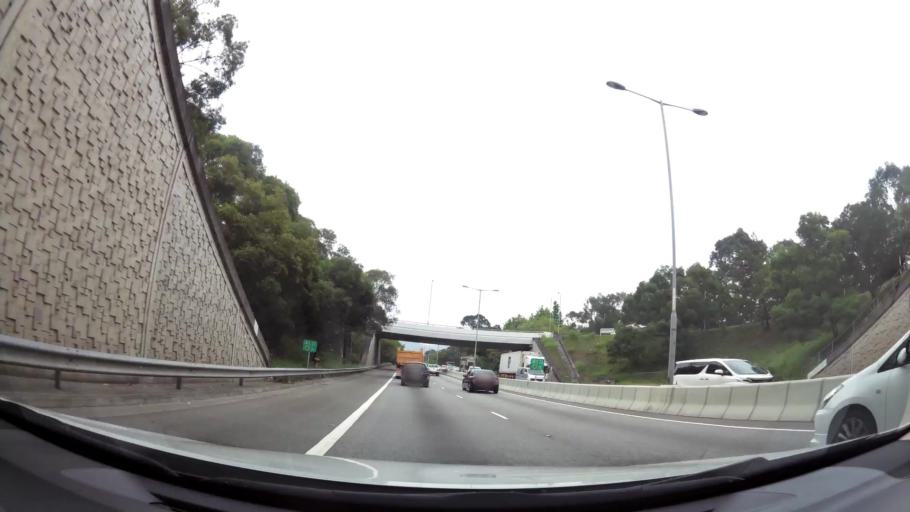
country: HK
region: Yuen Long
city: Yuen Long Kau Hui
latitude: 22.4360
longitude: 114.0354
